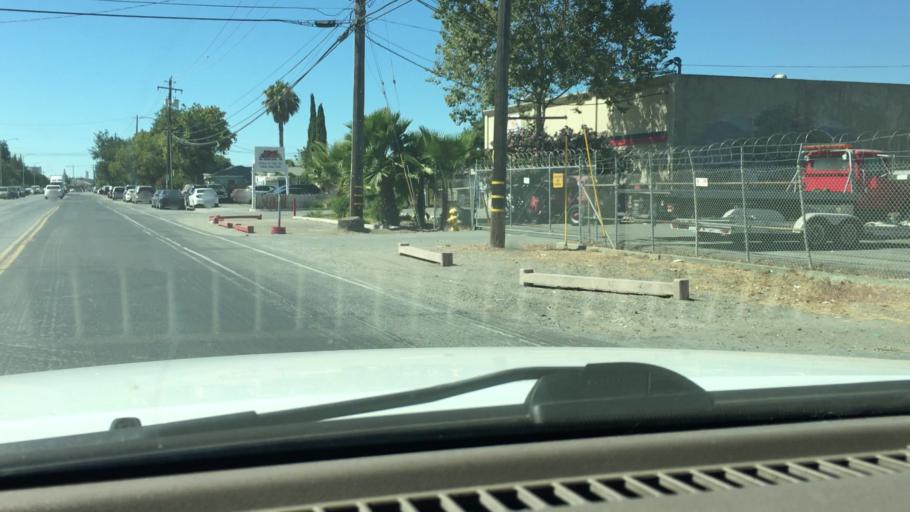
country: US
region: California
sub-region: Santa Clara County
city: Seven Trees
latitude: 37.3104
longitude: -121.8616
